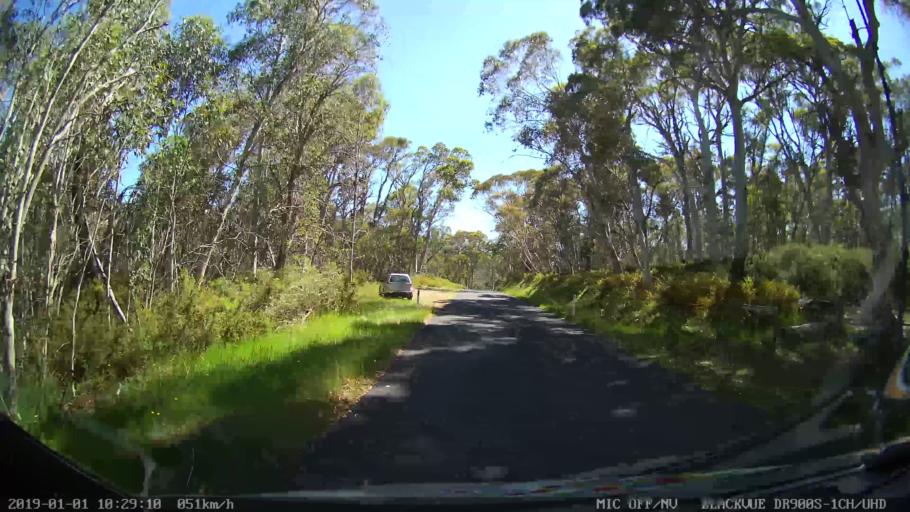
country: AU
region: New South Wales
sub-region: Snowy River
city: Jindabyne
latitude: -36.0560
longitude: 148.2457
